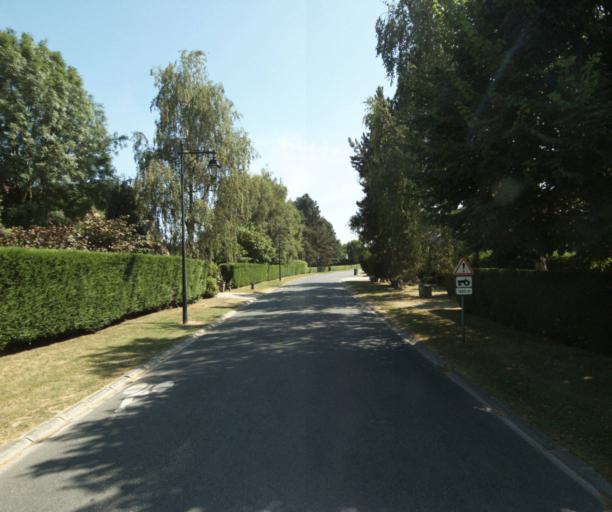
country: FR
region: Nord-Pas-de-Calais
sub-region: Departement du Nord
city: Linselles
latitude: 50.7173
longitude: 3.0732
